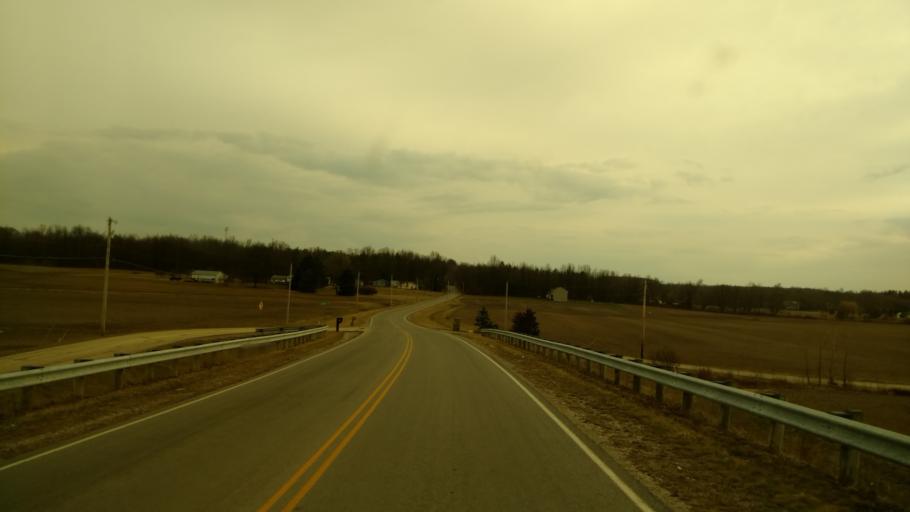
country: US
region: Ohio
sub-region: Crawford County
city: Crestline
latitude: 40.7735
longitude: -82.6674
